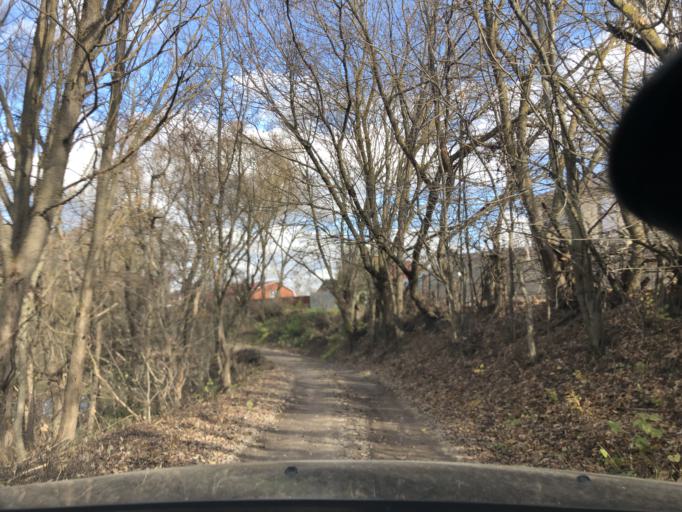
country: RU
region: Tula
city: Gorelki
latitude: 54.2960
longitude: 37.5613
